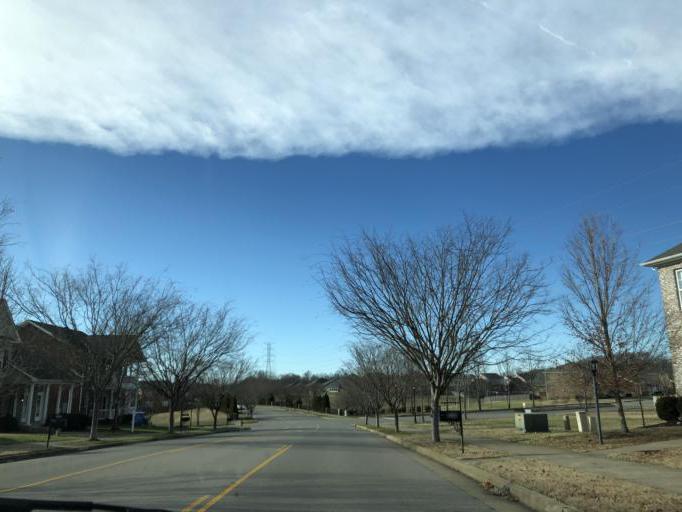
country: US
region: Tennessee
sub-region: Wilson County
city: Mount Juliet
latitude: 36.1590
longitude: -86.5706
